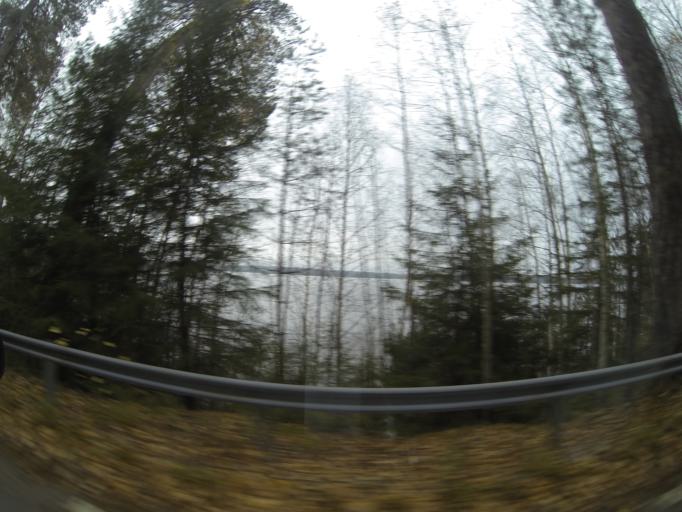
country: SE
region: Vaestmanland
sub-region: Surahammars Kommun
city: Surahammar
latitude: 59.6842
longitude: 16.0860
